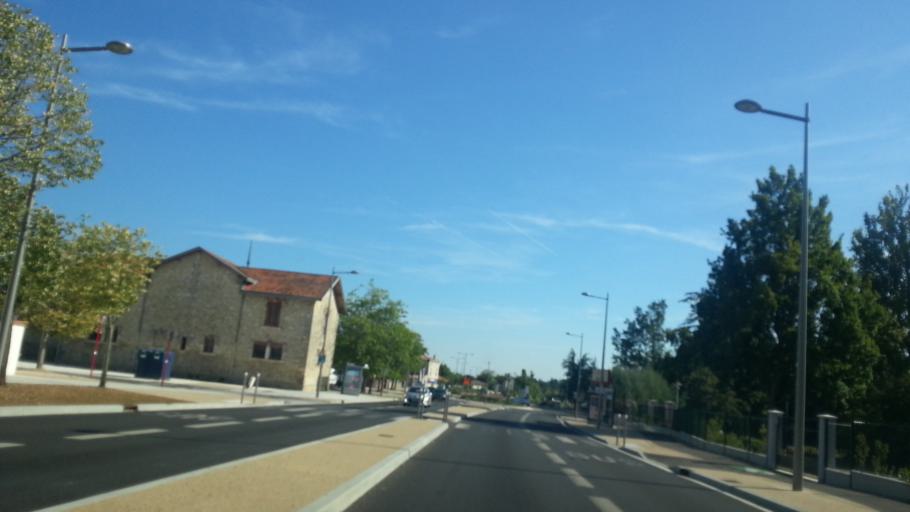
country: FR
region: Aquitaine
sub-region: Departement de la Gironde
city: Bassens
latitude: 44.8918
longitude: -0.5162
